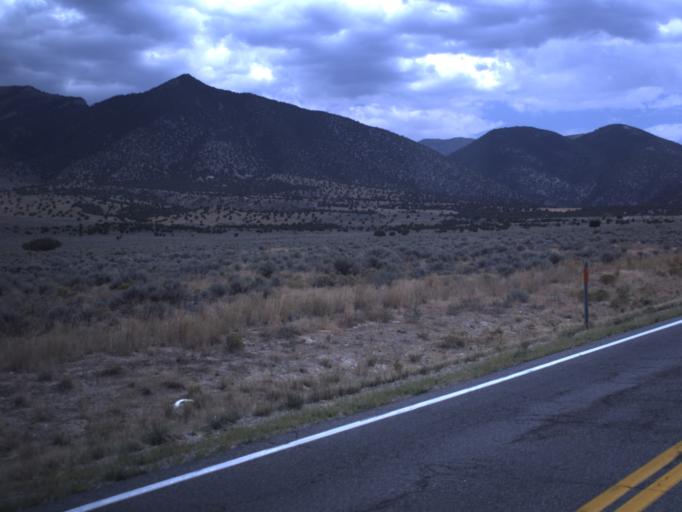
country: US
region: Utah
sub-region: Tooele County
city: Tooele
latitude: 40.3587
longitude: -112.3228
